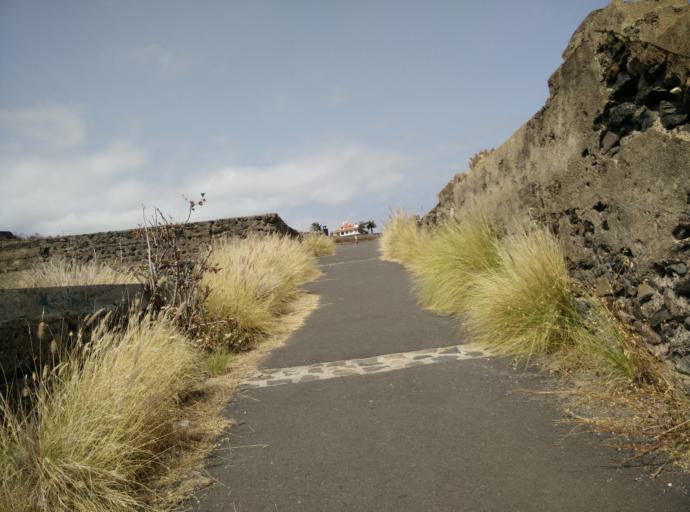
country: ES
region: Canary Islands
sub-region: Provincia de Santa Cruz de Tenerife
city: Puerto de la Cruz
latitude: 28.4163
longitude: -16.5238
